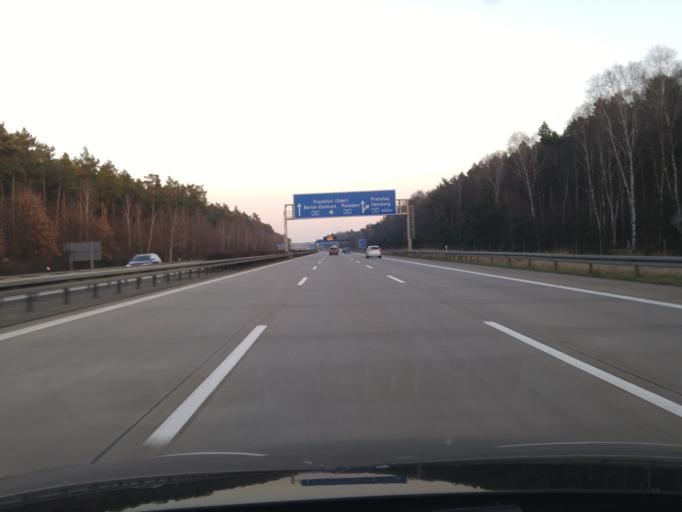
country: DE
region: Brandenburg
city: Gross Kreutz
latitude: 52.3395
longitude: 12.7828
